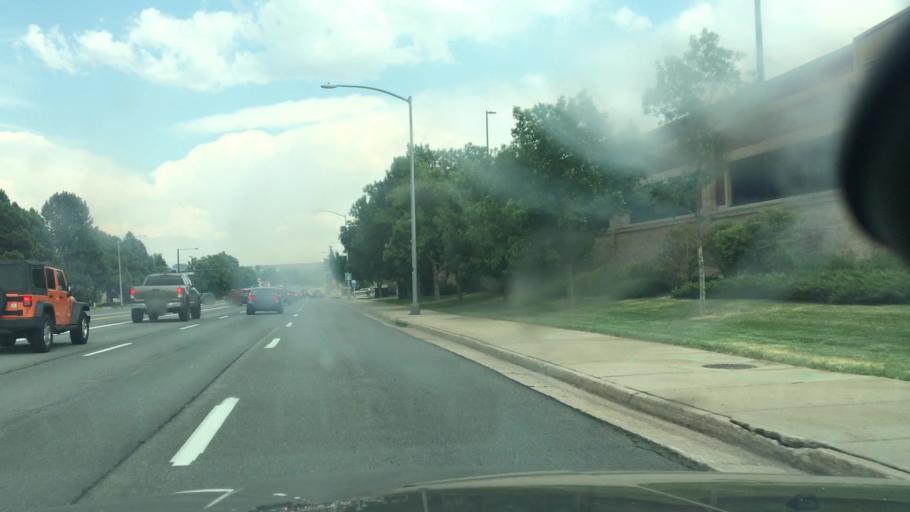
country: US
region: Colorado
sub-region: Arapahoe County
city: Castlewood
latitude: 39.6529
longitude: -104.8780
